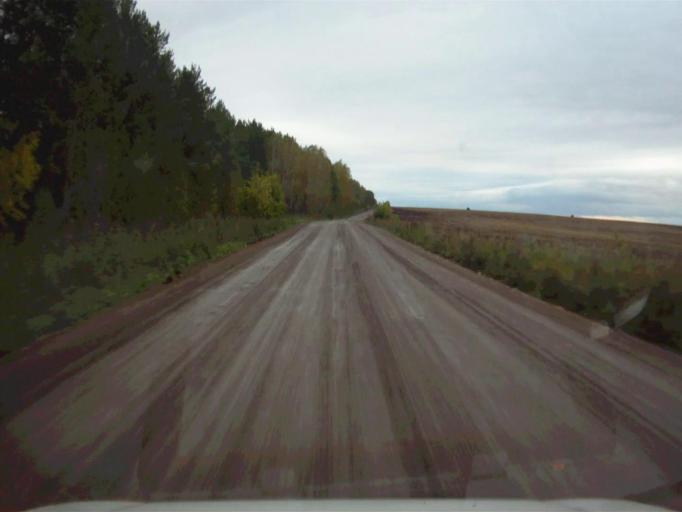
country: RU
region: Sverdlovsk
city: Mikhaylovsk
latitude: 56.1501
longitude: 59.2709
